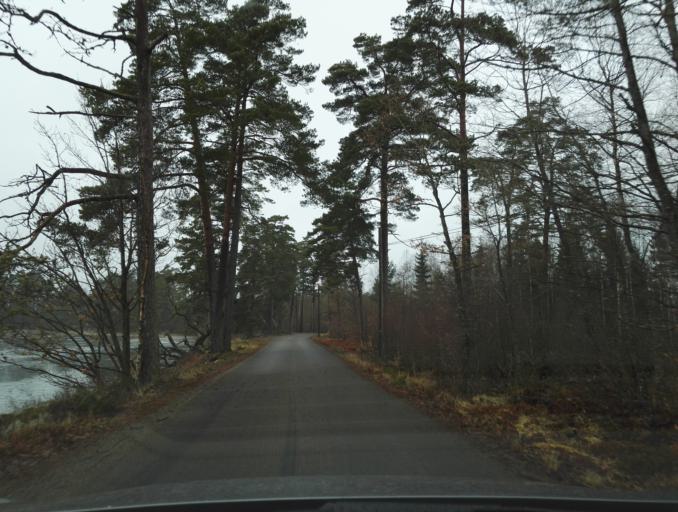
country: SE
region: Kronoberg
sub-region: Vaxjo Kommun
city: Vaexjoe
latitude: 56.9414
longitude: 14.7591
